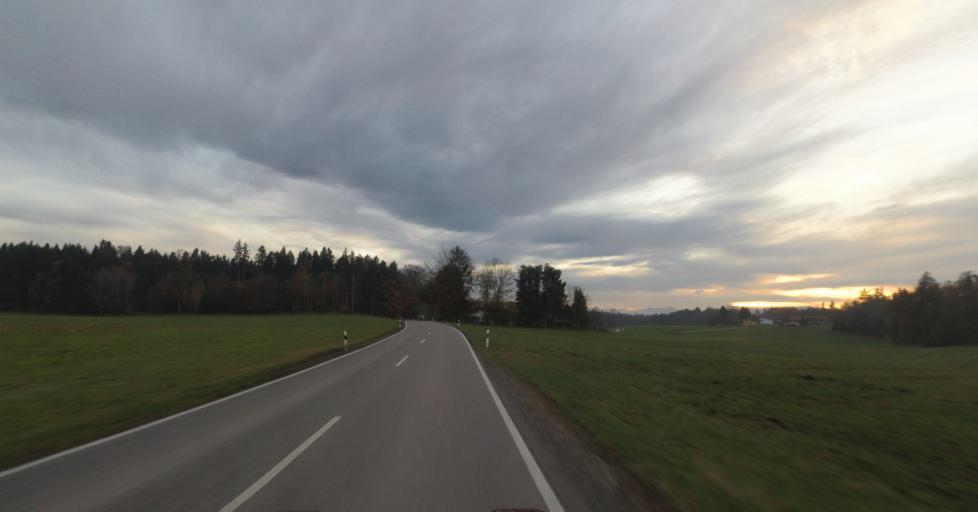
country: DE
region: Bavaria
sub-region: Upper Bavaria
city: Eggstatt
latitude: 47.9006
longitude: 12.3668
